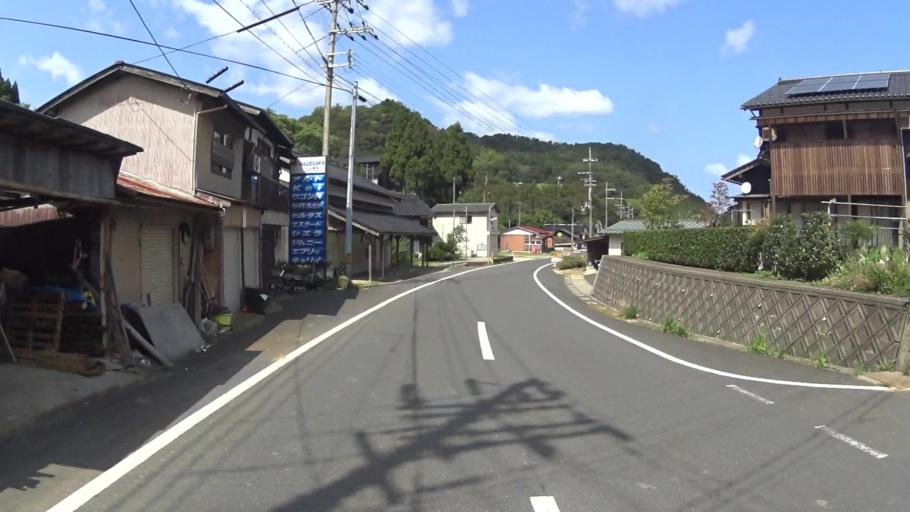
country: JP
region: Kyoto
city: Miyazu
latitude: 35.6969
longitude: 135.2507
